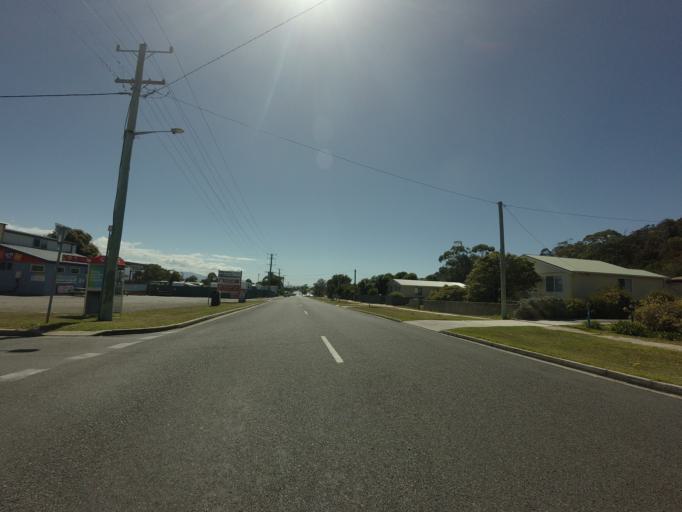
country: AU
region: Tasmania
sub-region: Break O'Day
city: St Helens
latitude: -41.8779
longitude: 148.3035
